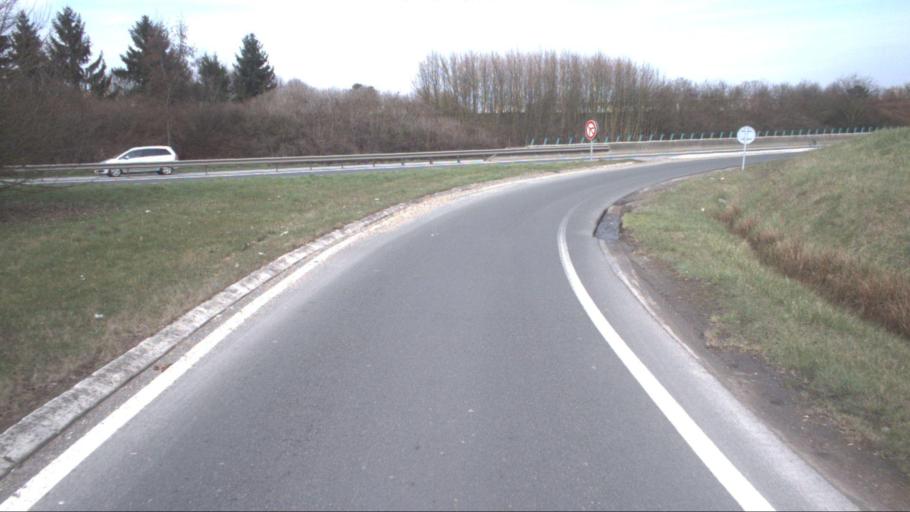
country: FR
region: Ile-de-France
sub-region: Departement des Yvelines
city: Rambouillet
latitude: 48.6462
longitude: 1.8435
